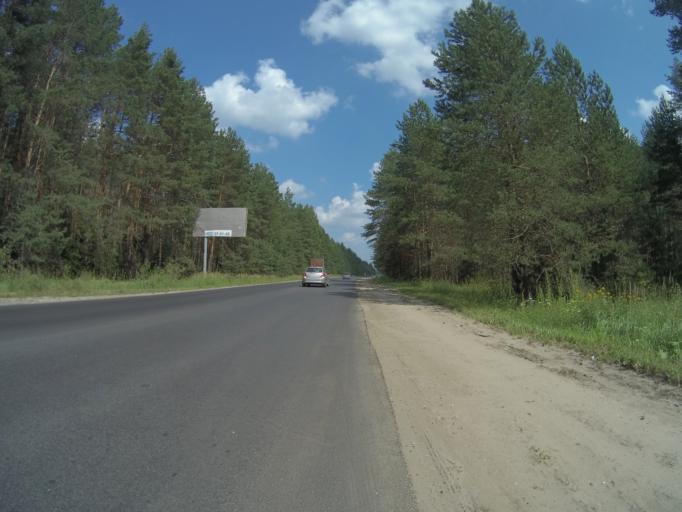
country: RU
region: Vladimir
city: Gus'-Khrustal'nyy
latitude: 55.6373
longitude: 40.7004
